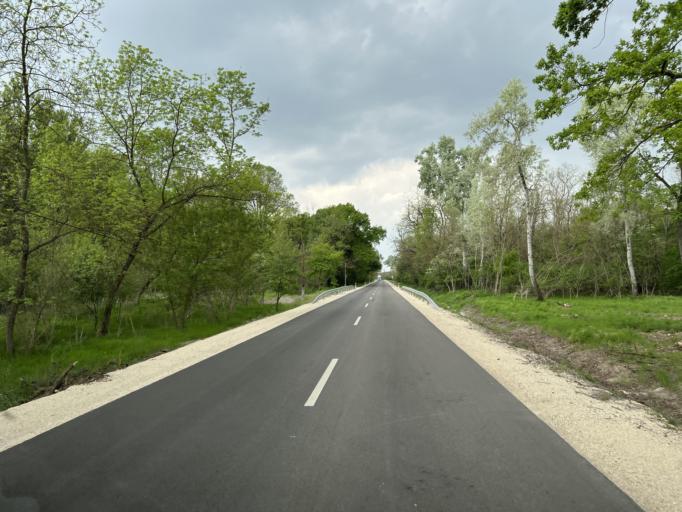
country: HU
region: Pest
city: Nagykoros
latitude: 47.0574
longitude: 19.7171
